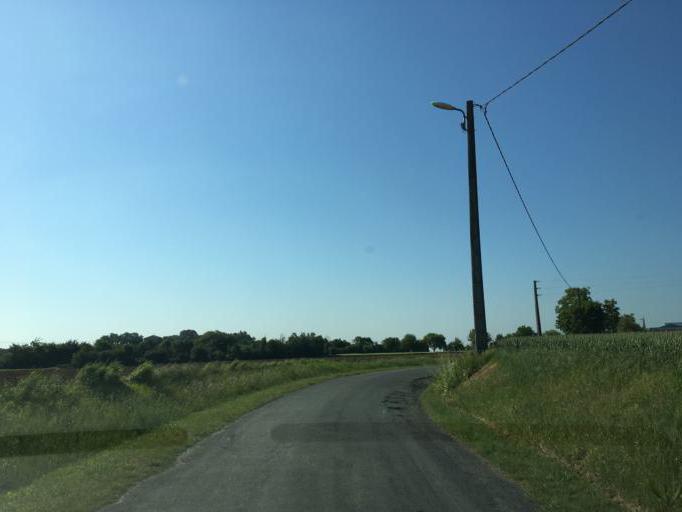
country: FR
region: Poitou-Charentes
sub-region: Departement des Deux-Sevres
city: Beauvoir-sur-Niort
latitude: 46.0921
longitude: -0.5059
